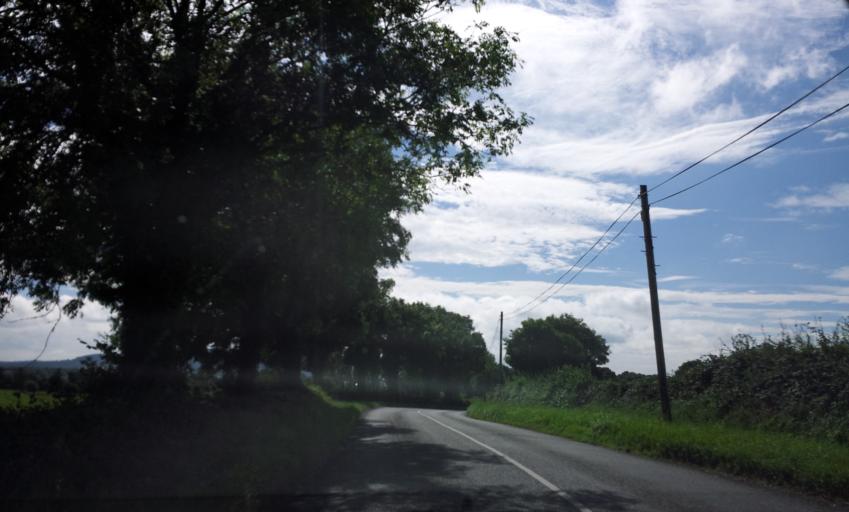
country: IE
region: Leinster
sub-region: Laois
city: Stradbally
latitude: 52.9908
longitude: -7.2203
